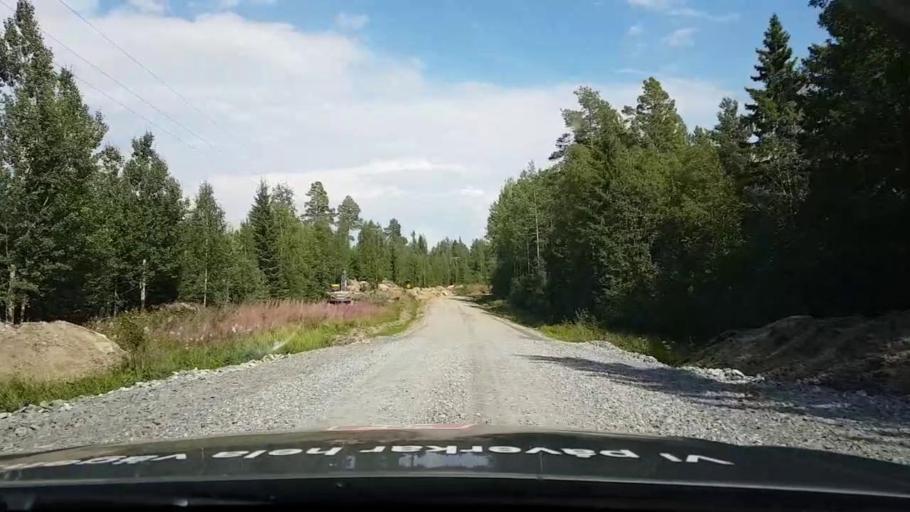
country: SE
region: Vaesternorrland
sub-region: Ange Kommun
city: Ange
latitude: 62.7695
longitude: 15.7464
